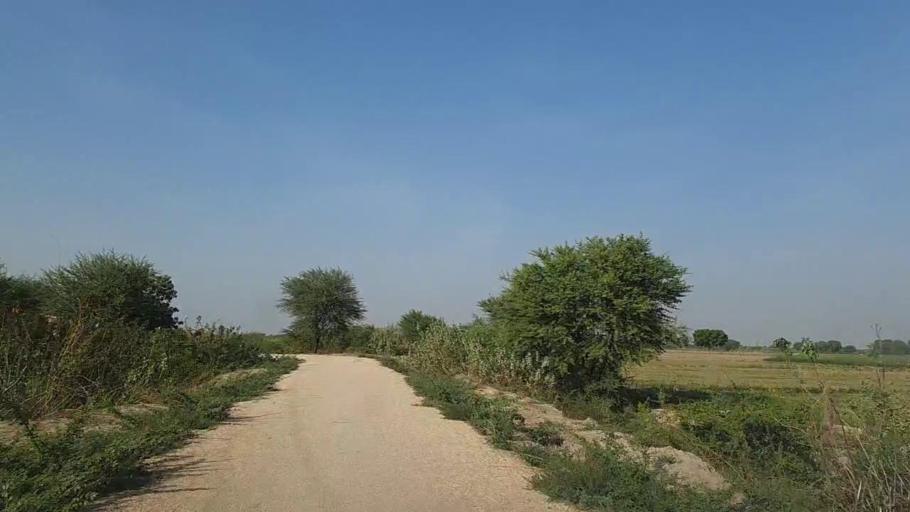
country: PK
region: Sindh
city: Naukot
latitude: 24.9373
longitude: 69.4589
